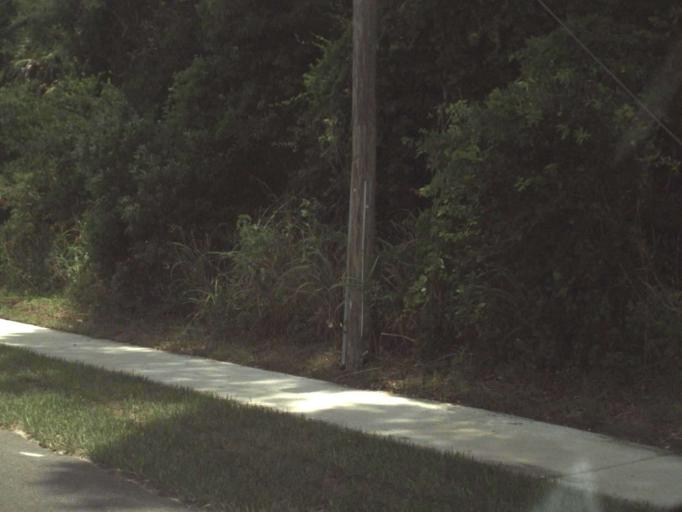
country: US
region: Florida
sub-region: Seminole County
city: Oviedo
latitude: 28.6703
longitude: -81.2163
